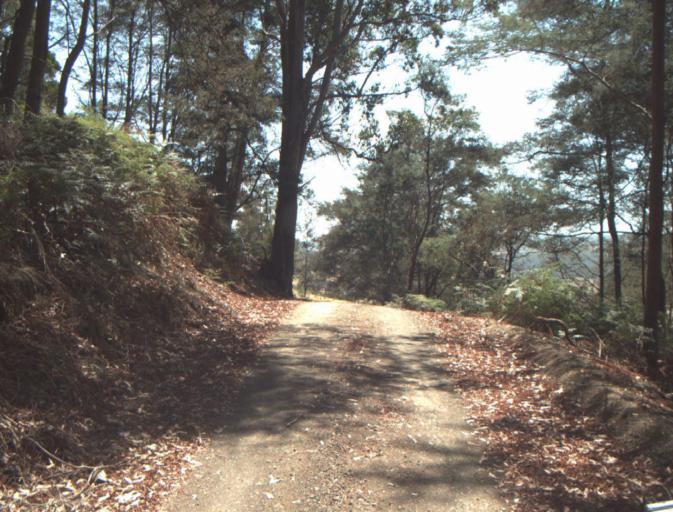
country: AU
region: Tasmania
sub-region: Launceston
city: Mayfield
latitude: -41.2444
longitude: 147.1170
